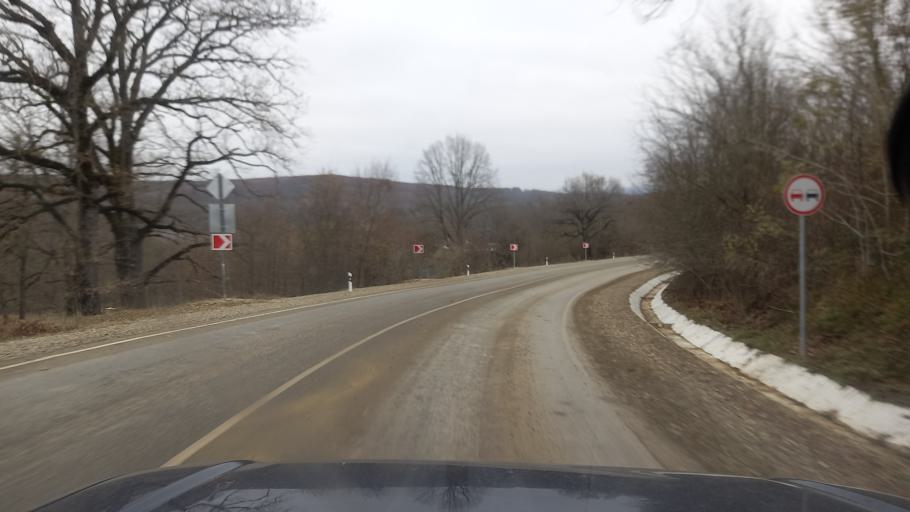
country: RU
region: Krasnodarskiy
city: Saratovskaya
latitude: 44.5459
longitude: 39.2897
